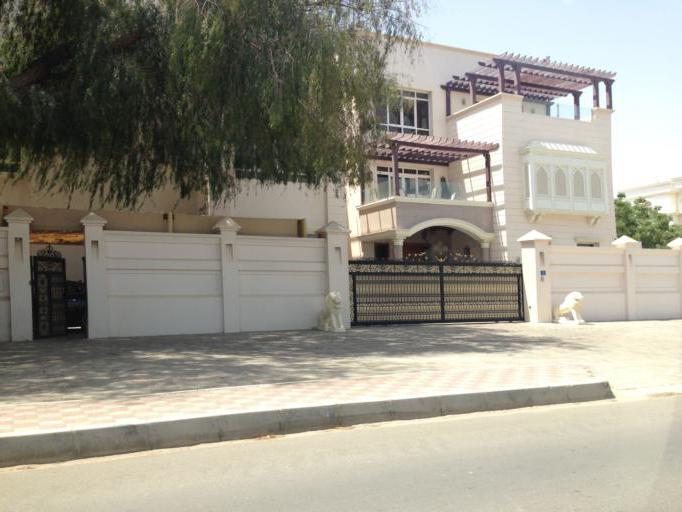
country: OM
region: Muhafazat Masqat
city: Bawshar
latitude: 23.6039
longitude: 58.3630
